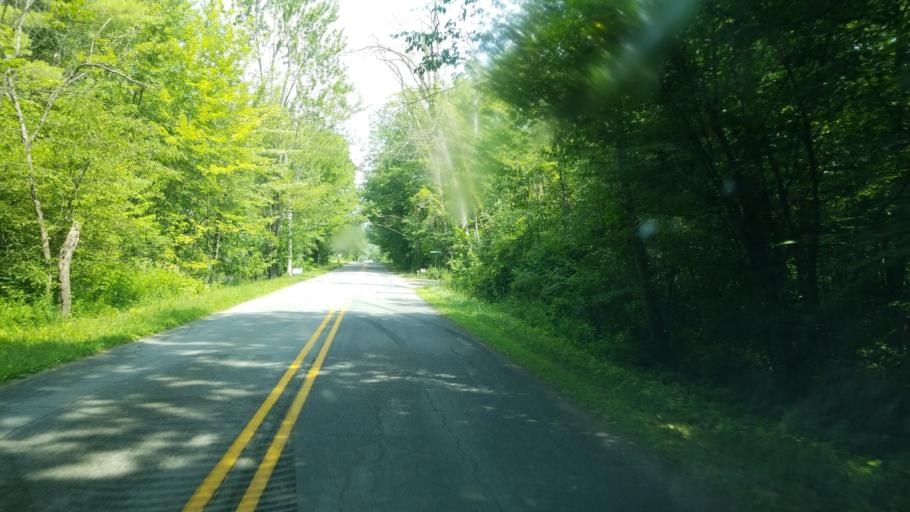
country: US
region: Michigan
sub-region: Kent County
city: Cedar Springs
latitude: 43.2526
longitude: -85.5112
